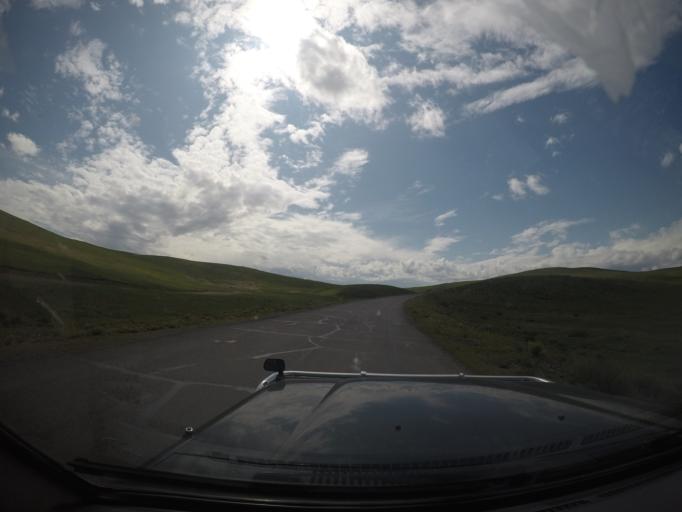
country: MN
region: Hentiy
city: Bayanbulag
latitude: 47.4470
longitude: 109.7797
